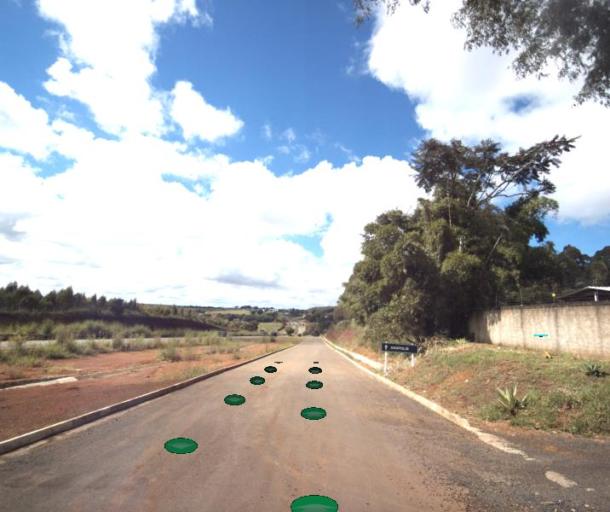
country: BR
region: Goias
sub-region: Anapolis
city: Anapolis
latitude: -16.2387
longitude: -49.0052
